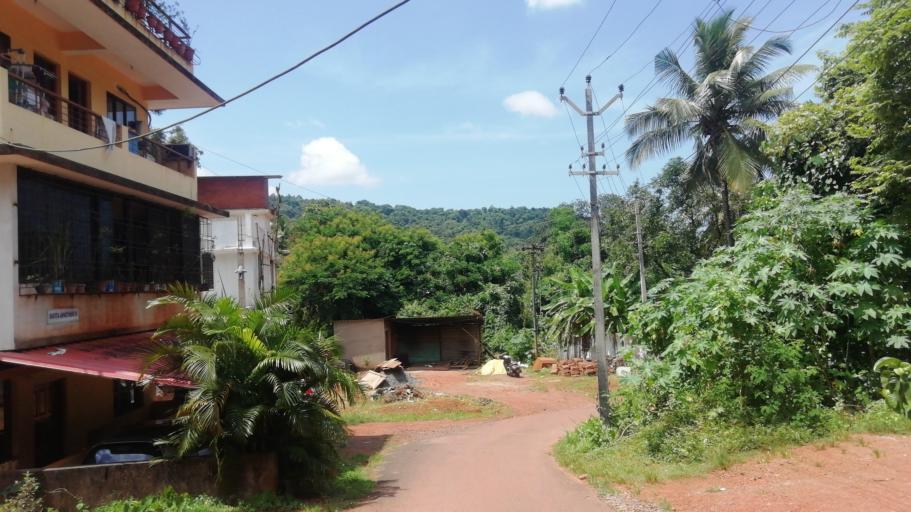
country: IN
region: Goa
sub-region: North Goa
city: Queula
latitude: 15.3860
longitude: 74.0015
